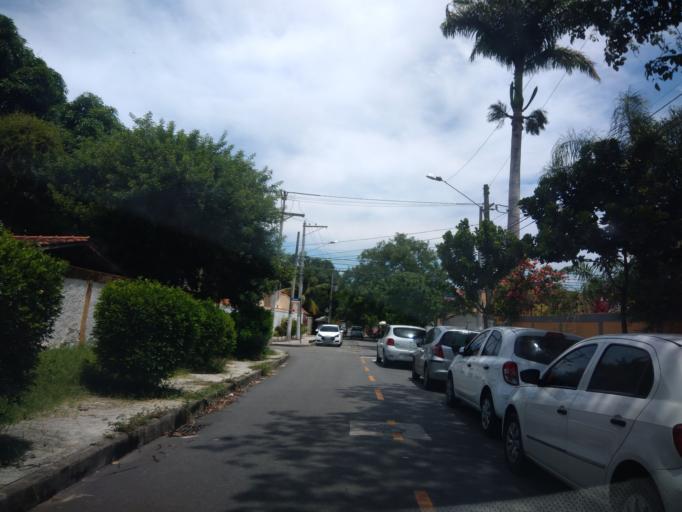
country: BR
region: Rio de Janeiro
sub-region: Niteroi
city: Niteroi
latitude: -22.9315
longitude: -43.0715
